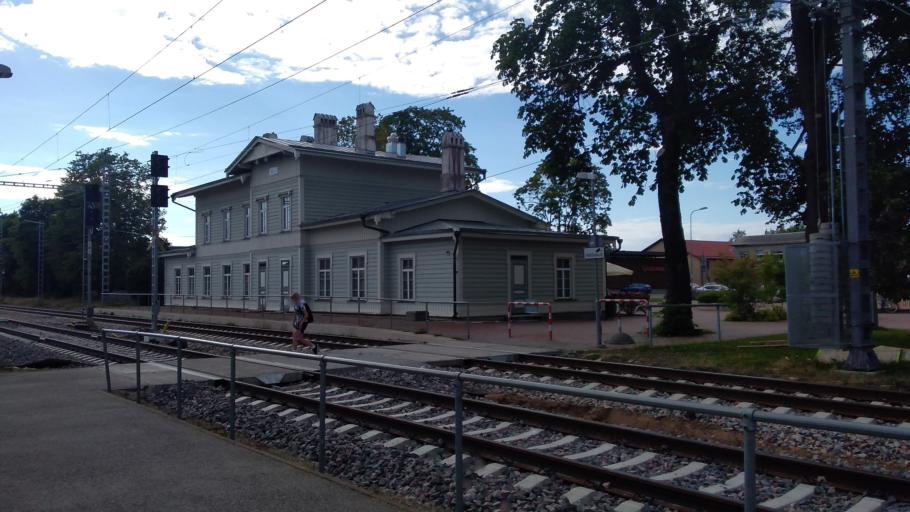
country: EE
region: Harju
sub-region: Keila linn
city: Keila
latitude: 59.3061
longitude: 24.4156
